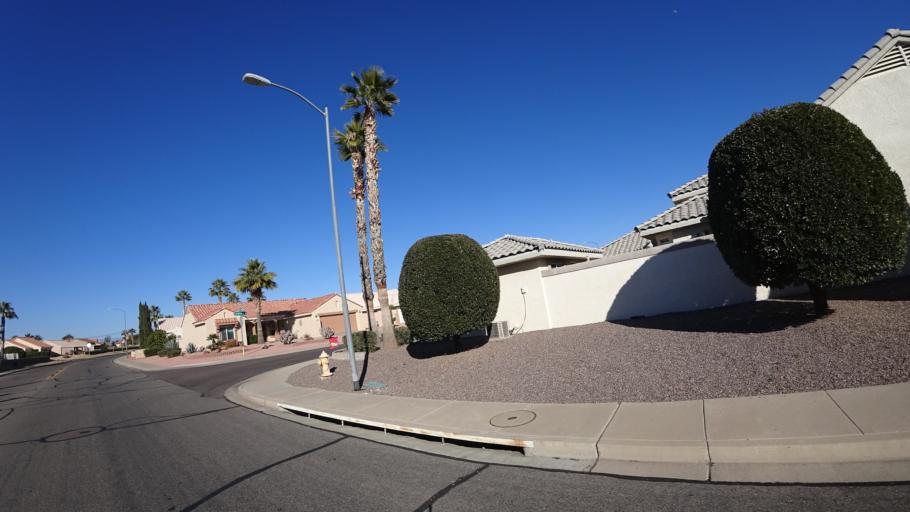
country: US
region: Arizona
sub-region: Maricopa County
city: Sun City West
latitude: 33.6895
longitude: -112.3815
